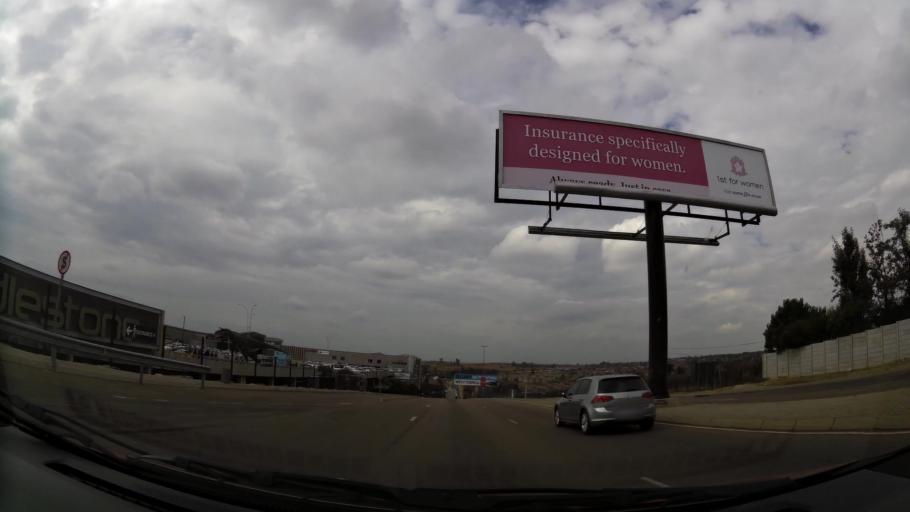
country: ZA
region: Gauteng
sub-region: West Rand District Municipality
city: Muldersdriseloop
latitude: -26.0621
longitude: 27.8361
